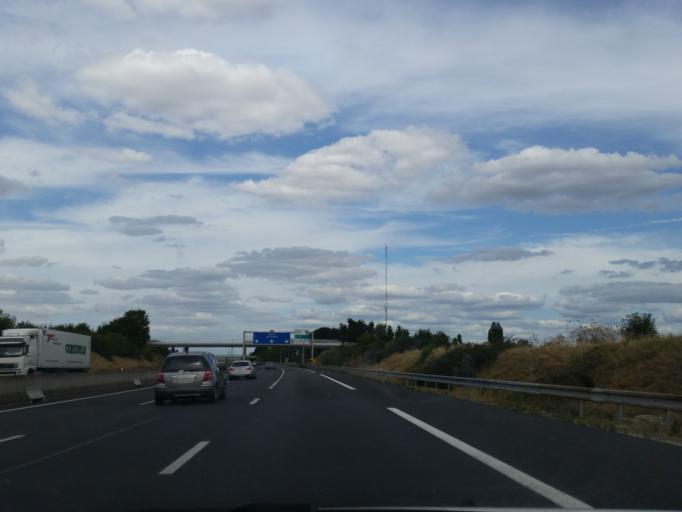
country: FR
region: Centre
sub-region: Departement du Loir-et-Cher
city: Villebarou
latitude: 47.6213
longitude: 1.3401
